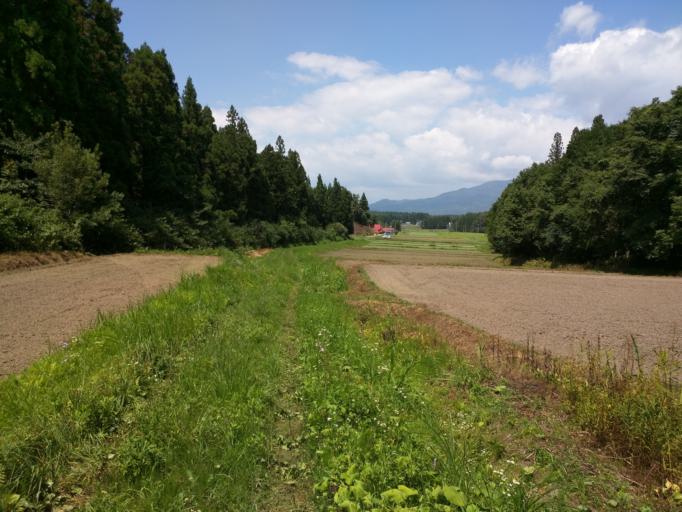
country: JP
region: Fukushima
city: Inawashiro
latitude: 37.5061
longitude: 139.9911
